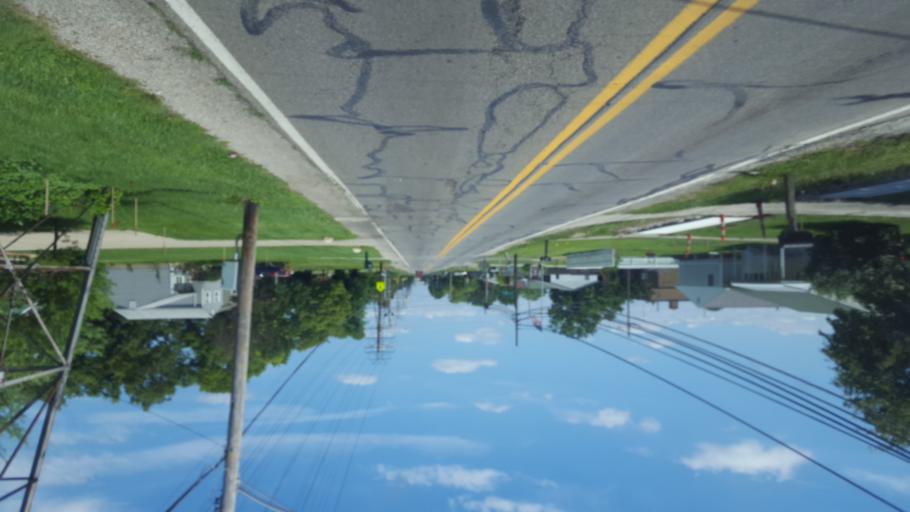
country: US
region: Ohio
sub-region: Franklin County
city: Obetz
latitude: 39.9001
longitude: -82.9863
